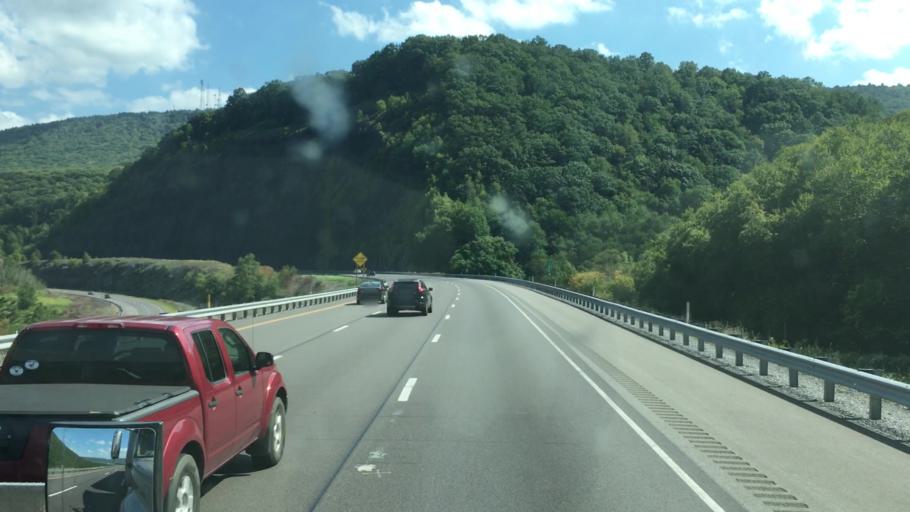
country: US
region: Pennsylvania
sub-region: Clinton County
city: Castanea
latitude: 41.0634
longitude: -77.3972
